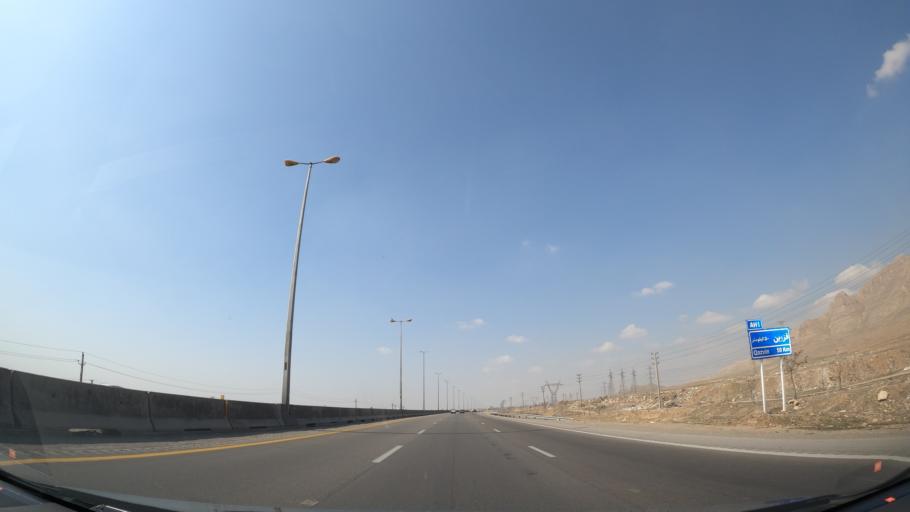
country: IR
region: Qazvin
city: Abyek
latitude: 36.0526
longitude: 50.5143
